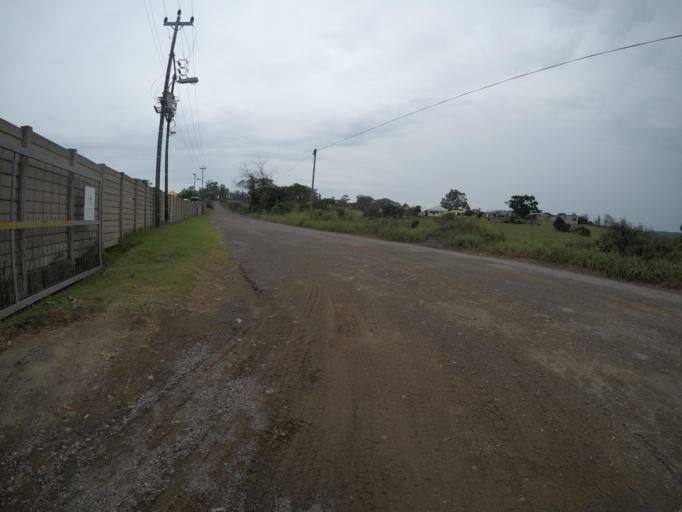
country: ZA
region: Eastern Cape
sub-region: Buffalo City Metropolitan Municipality
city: East London
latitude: -32.9591
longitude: 27.8430
